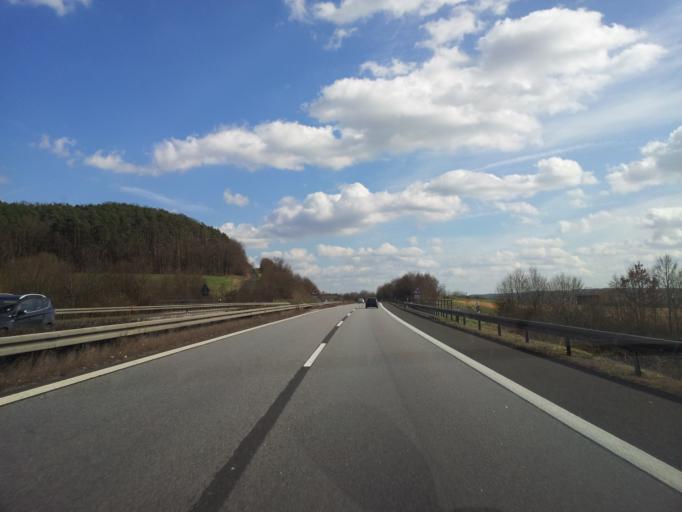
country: DE
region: Bavaria
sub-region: Regierungsbezirk Unterfranken
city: Stettfeld
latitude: 49.9558
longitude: 10.7464
